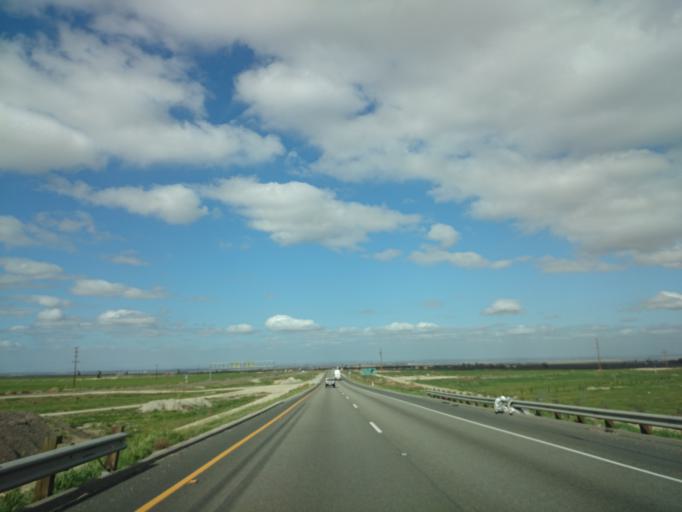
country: US
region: California
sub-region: Kern County
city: Frazier Park
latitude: 35.0201
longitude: -118.9573
